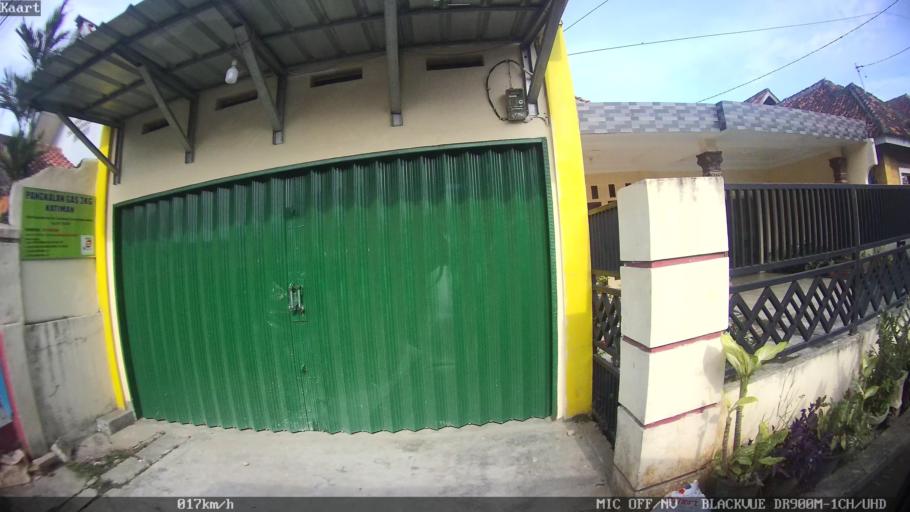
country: ID
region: Lampung
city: Bandarlampung
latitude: -5.4106
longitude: 105.2657
